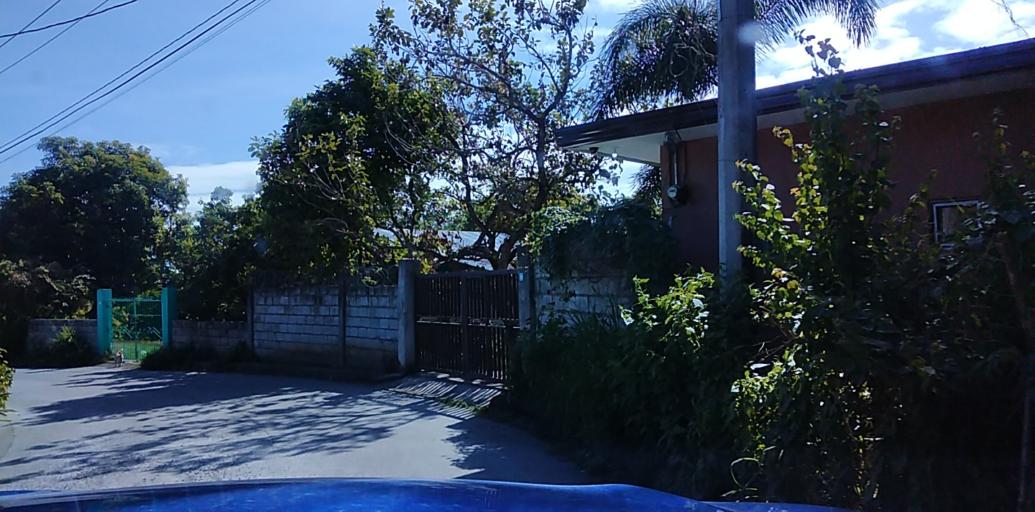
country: PH
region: Central Luzon
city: Santol
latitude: 15.1688
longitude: 120.5000
